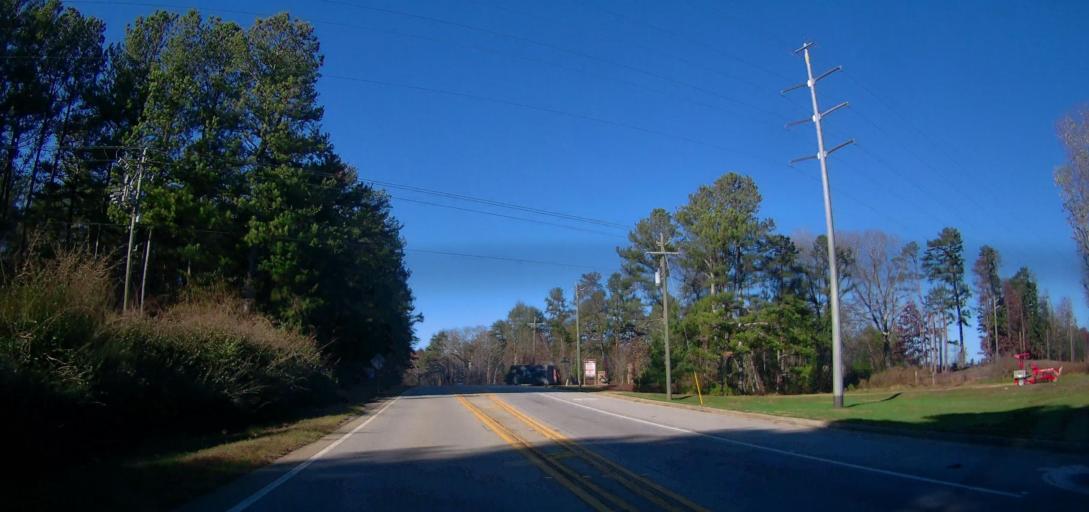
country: US
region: Georgia
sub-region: Hall County
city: Lula
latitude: 34.4032
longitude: -83.6983
